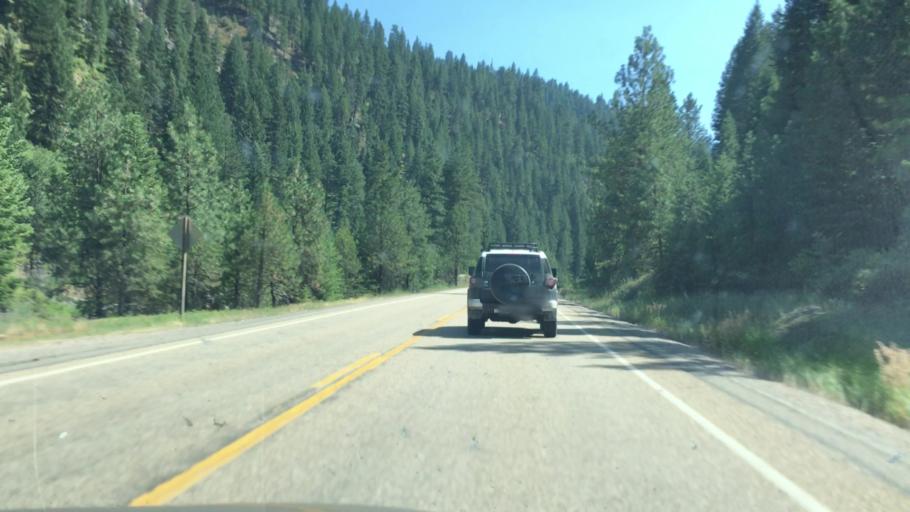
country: US
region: Idaho
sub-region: Valley County
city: Cascade
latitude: 44.2133
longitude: -116.1072
